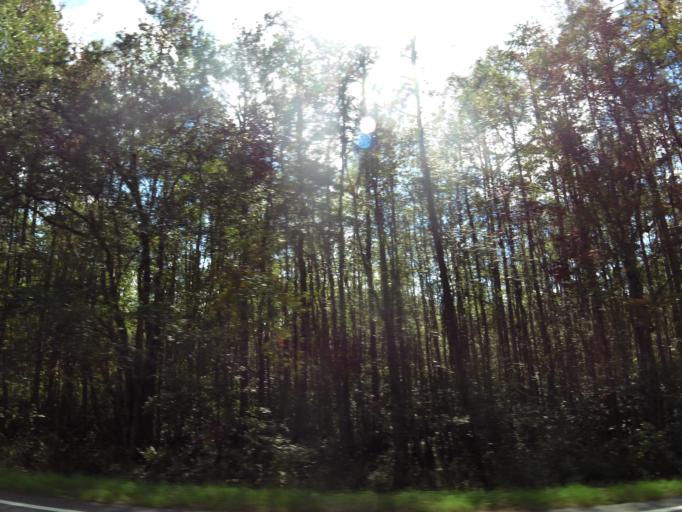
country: US
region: Georgia
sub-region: Echols County
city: Statenville
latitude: 30.7289
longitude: -83.0824
